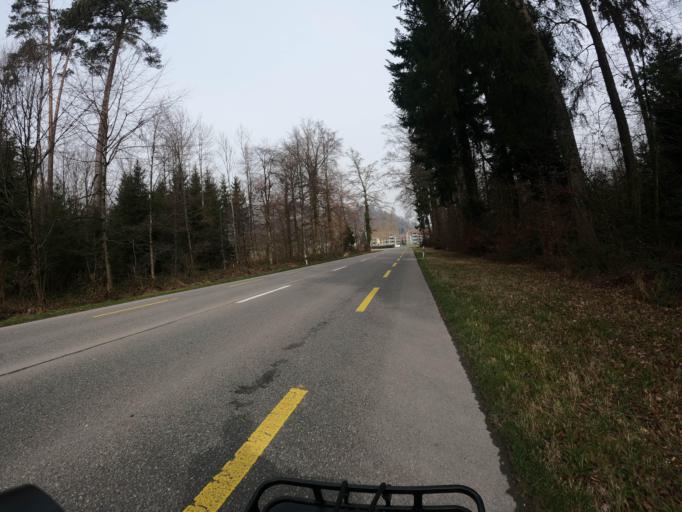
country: CH
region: Aargau
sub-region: Bezirk Lenzburg
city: Othmarsingen
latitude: 47.4135
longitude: 8.2138
